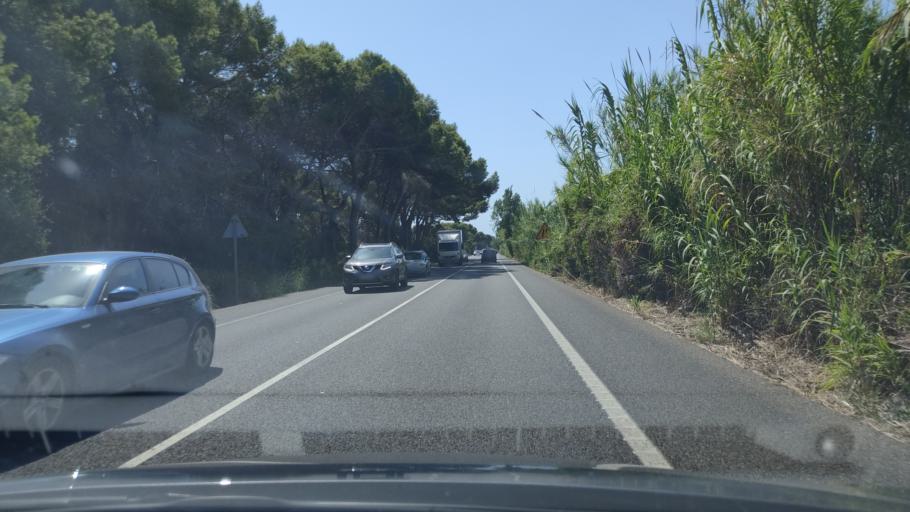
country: ES
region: Valencia
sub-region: Provincia de Valencia
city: Sollana
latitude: 39.3525
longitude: -0.3245
